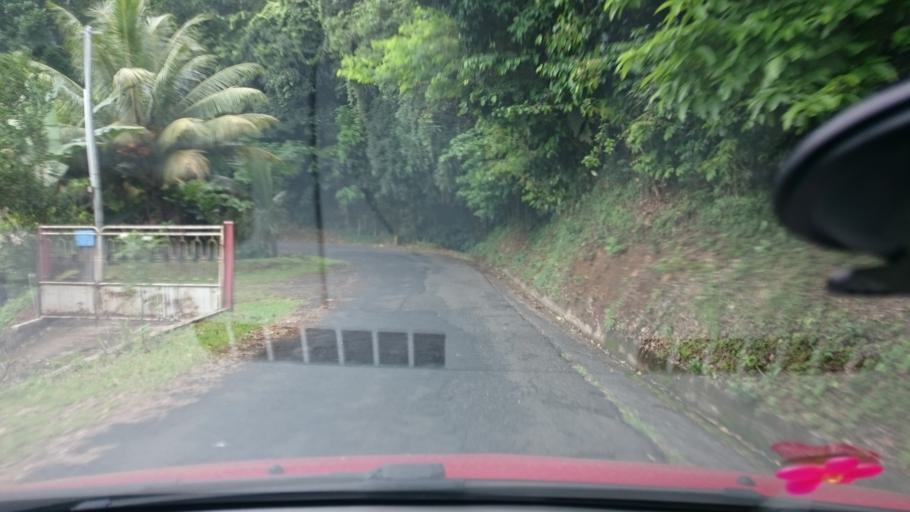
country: MQ
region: Martinique
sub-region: Martinique
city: Riviere-Pilote
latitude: 14.5009
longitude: -60.9186
